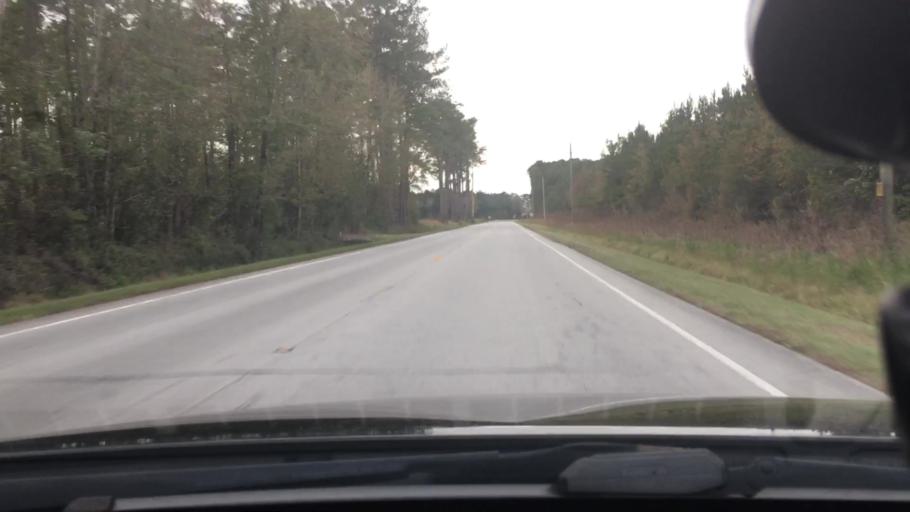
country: US
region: North Carolina
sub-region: Craven County
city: Vanceboro
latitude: 35.4132
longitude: -77.2503
